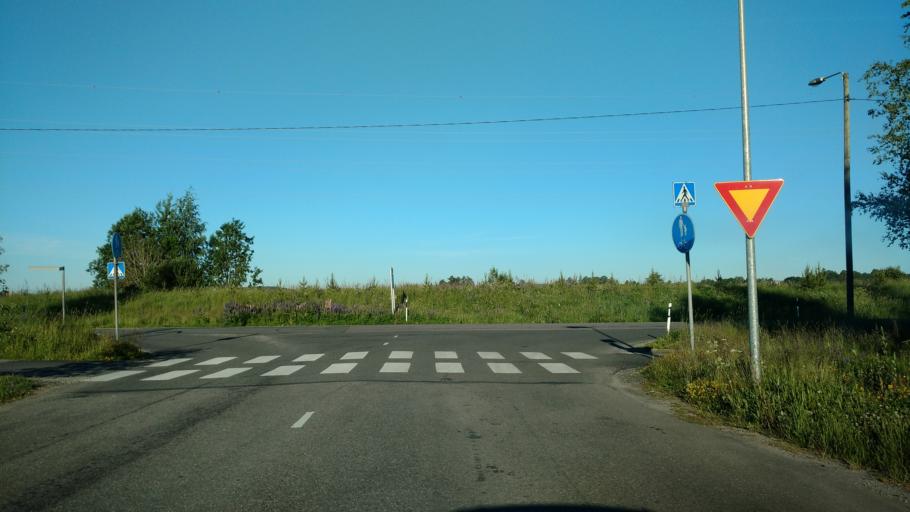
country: FI
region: Varsinais-Suomi
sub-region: Salo
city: Halikko
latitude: 60.3813
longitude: 23.1033
